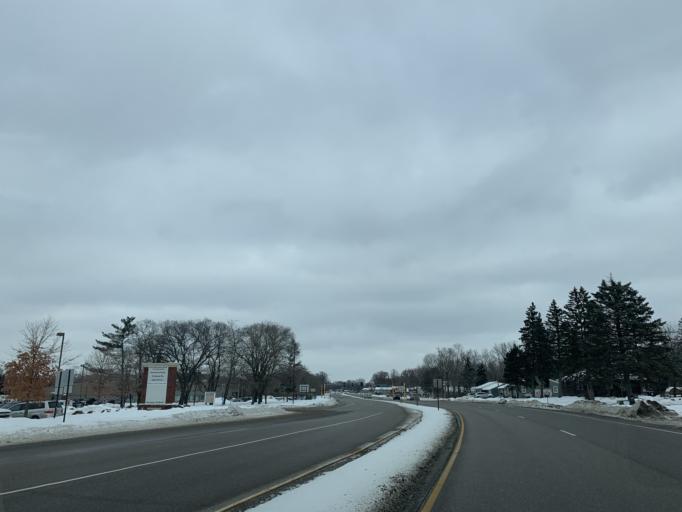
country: US
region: Minnesota
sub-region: Anoka County
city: Coon Rapids
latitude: 45.1550
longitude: -93.2732
